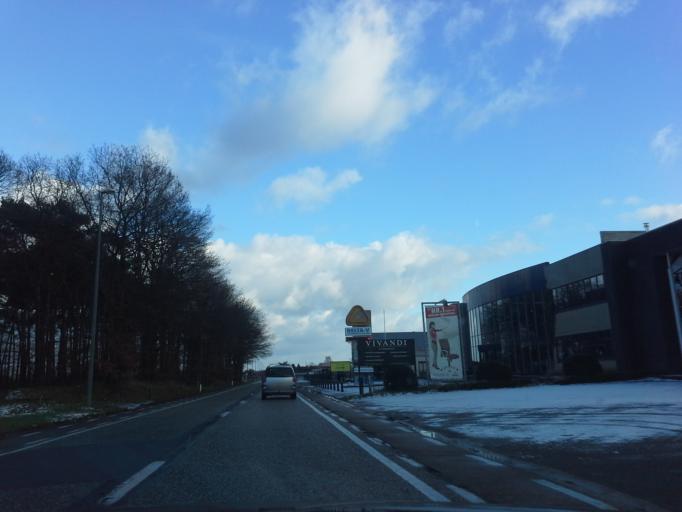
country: BE
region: Flanders
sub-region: Provincie Limburg
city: Neerpelt
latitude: 51.2458
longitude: 5.5041
